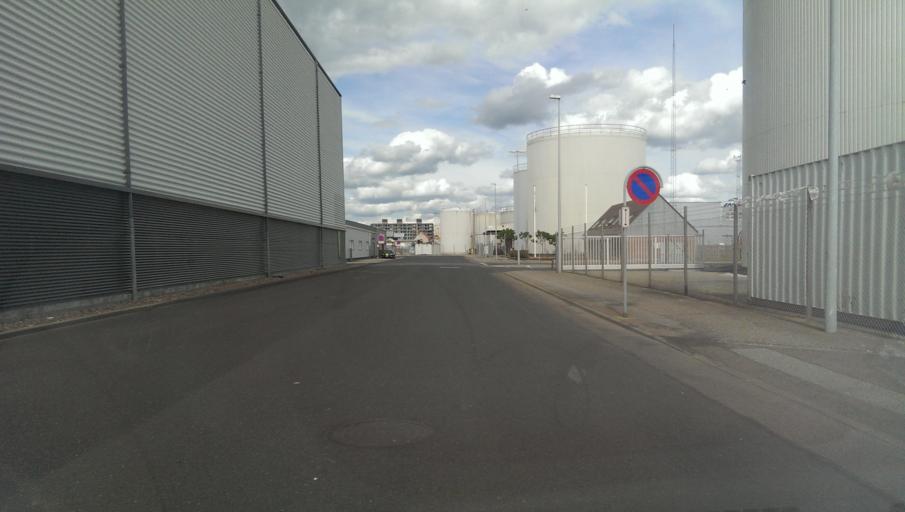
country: DK
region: South Denmark
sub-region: Esbjerg Kommune
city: Esbjerg
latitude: 55.4714
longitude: 8.4271
